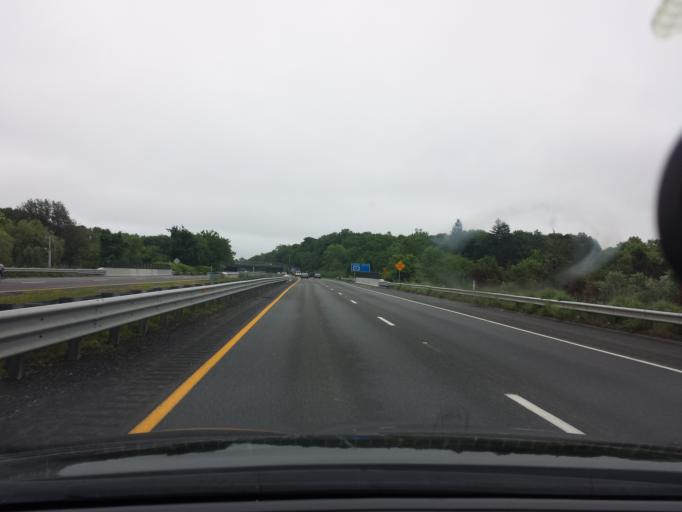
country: US
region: Massachusetts
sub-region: Bristol County
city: Fairhaven
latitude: 41.6544
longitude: -70.9148
